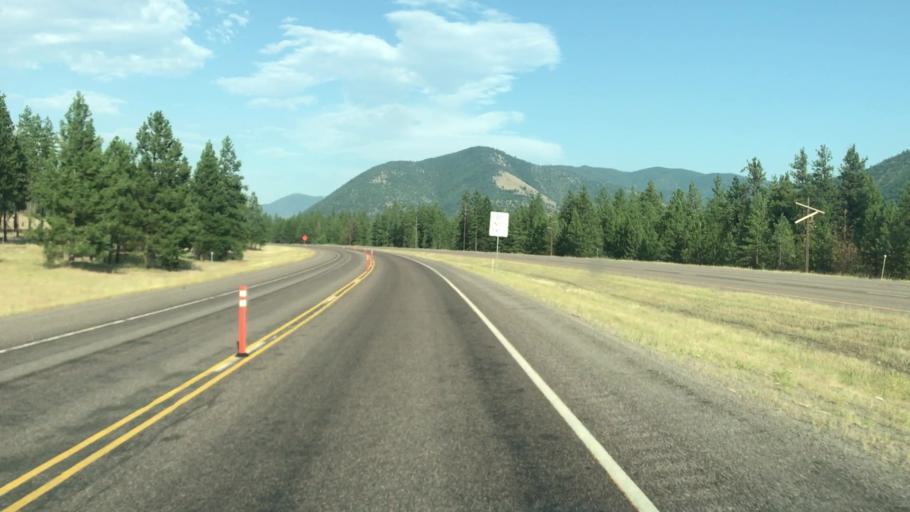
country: US
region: Montana
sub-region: Mineral County
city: Superior
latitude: 47.0120
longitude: -114.7231
